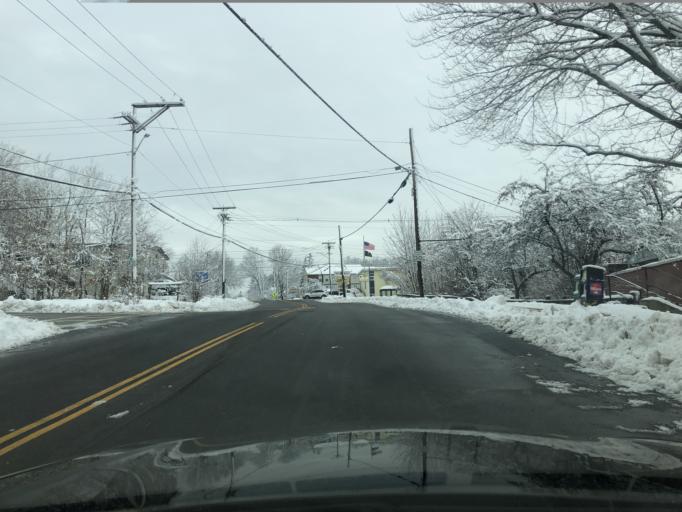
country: US
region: New Hampshire
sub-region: Strafford County
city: Somersworth
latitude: 43.2607
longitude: -70.8632
